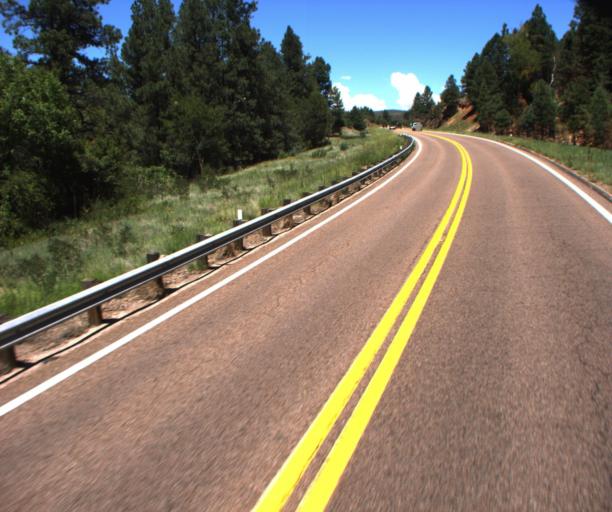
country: US
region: Arizona
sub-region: Navajo County
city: Linden
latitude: 34.0712
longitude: -110.1935
